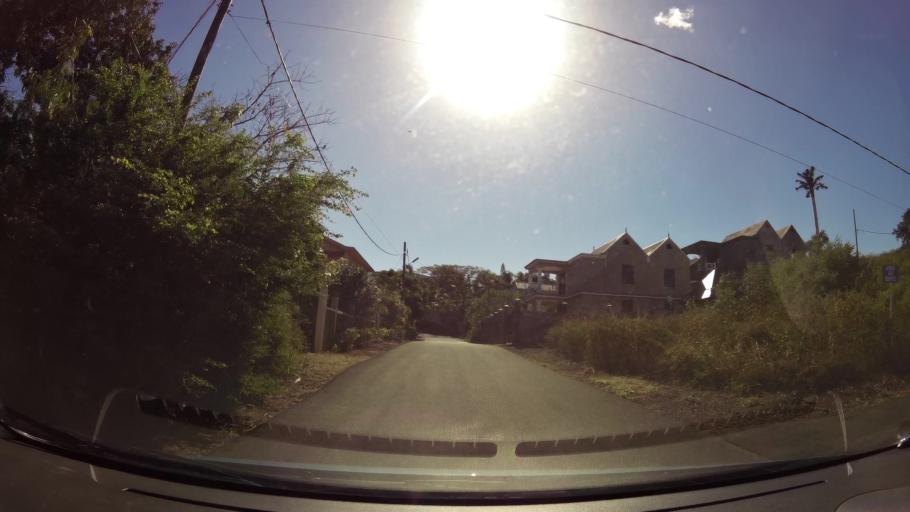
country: MU
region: Black River
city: Flic en Flac
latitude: -20.2709
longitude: 57.3750
